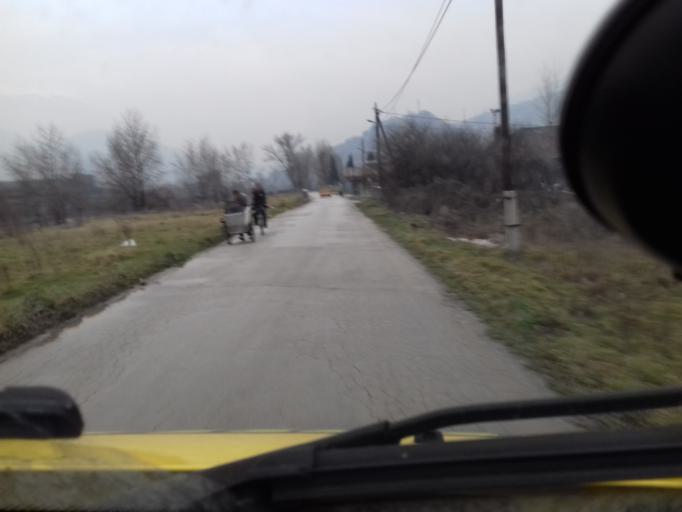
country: BA
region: Federation of Bosnia and Herzegovina
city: Zenica
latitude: 44.2229
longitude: 17.9082
